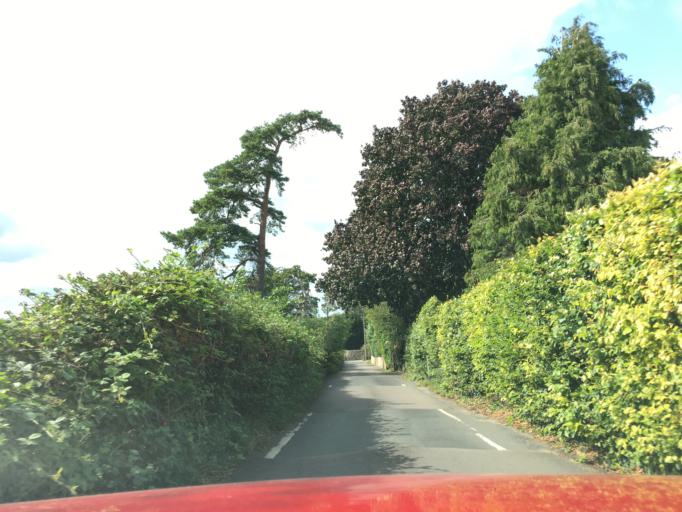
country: GB
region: England
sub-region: Kent
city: Maidstone
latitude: 51.2533
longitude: 0.5207
